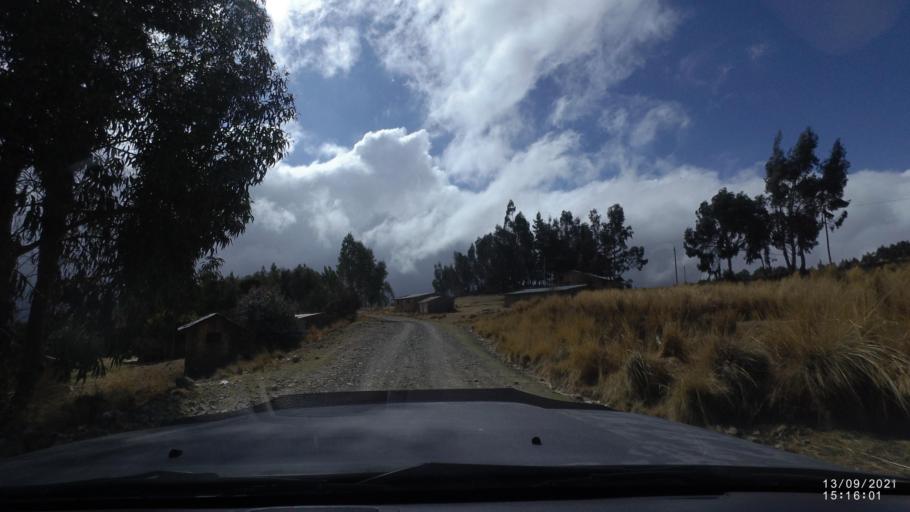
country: BO
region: Cochabamba
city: Colomi
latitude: -17.3671
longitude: -65.7935
